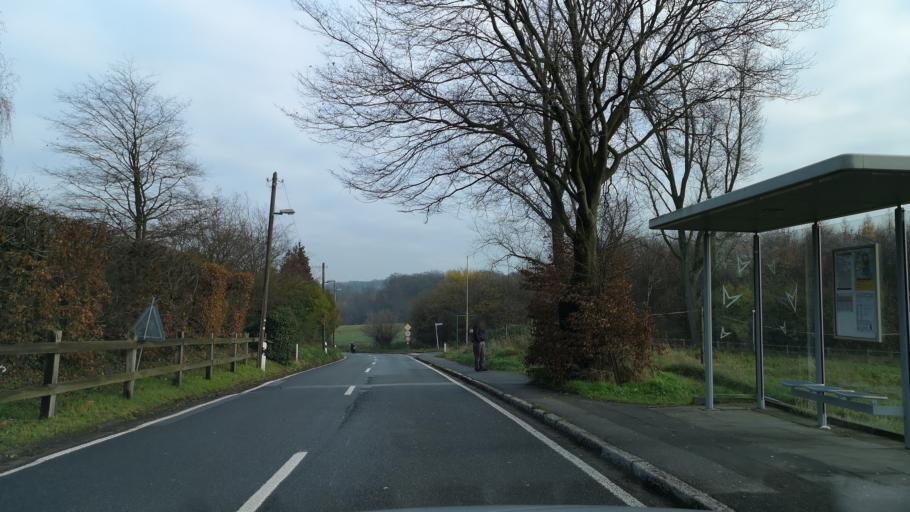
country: DE
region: North Rhine-Westphalia
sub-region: Regierungsbezirk Dusseldorf
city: Velbert
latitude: 51.3828
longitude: 7.0489
